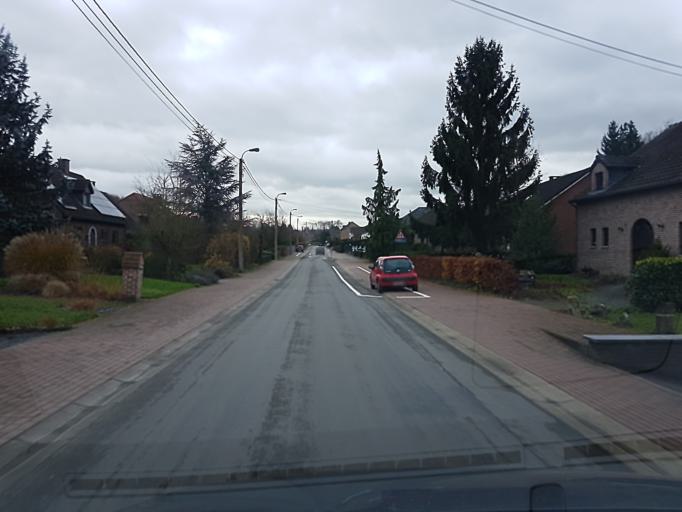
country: BE
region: Wallonia
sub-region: Province de Liege
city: Dalhem
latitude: 50.7116
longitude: 5.7329
